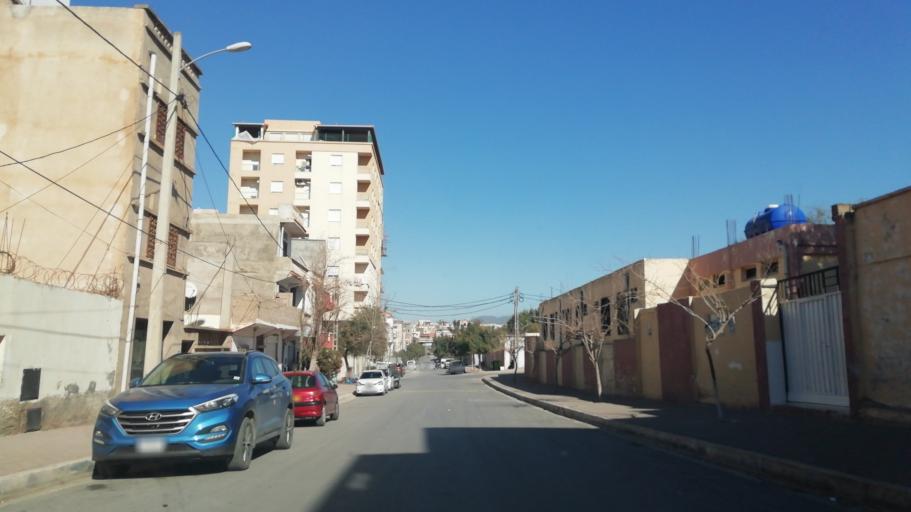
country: DZ
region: Oran
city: Bir el Djir
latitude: 35.7267
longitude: -0.5783
